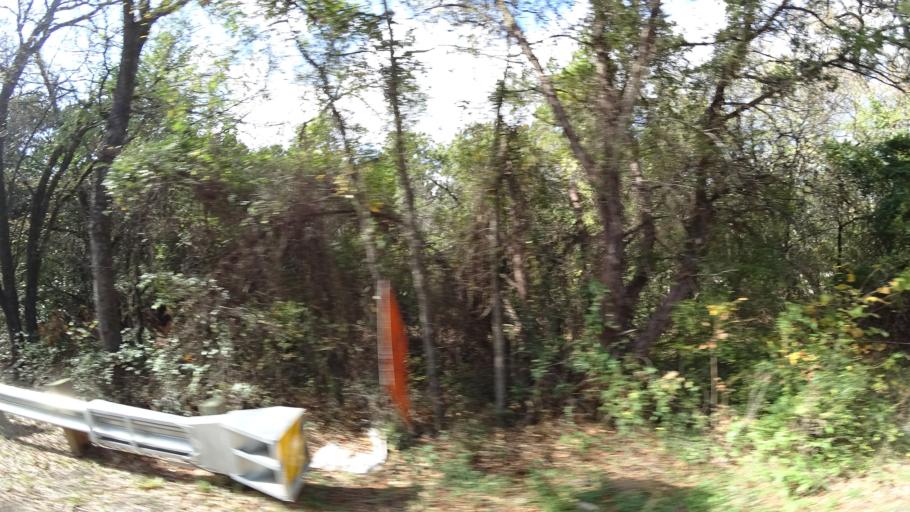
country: US
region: Texas
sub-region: Williamson County
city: Jollyville
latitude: 30.4100
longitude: -97.7924
